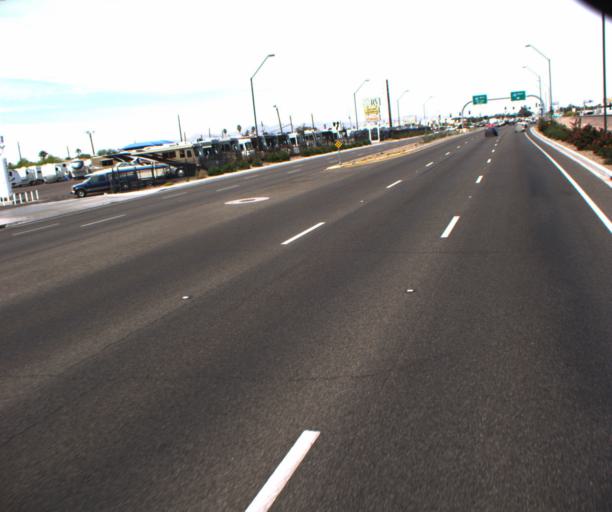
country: US
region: Arizona
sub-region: Maricopa County
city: Peoria
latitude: 33.5919
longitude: -112.2523
